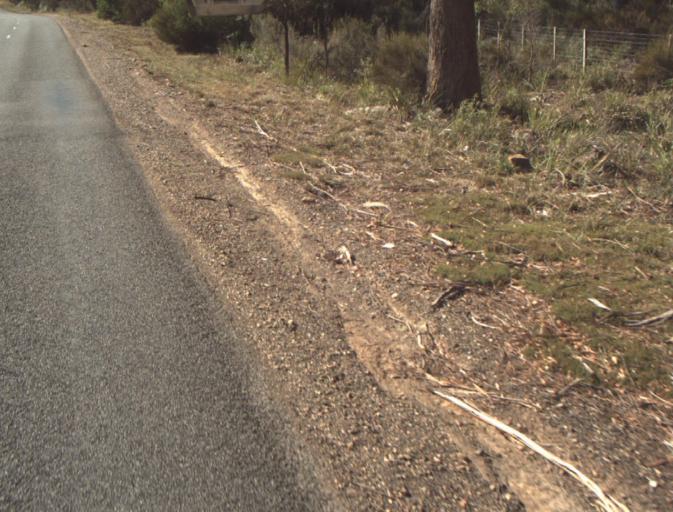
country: AU
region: Tasmania
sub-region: Launceston
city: Mayfield
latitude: -41.3062
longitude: 147.1337
